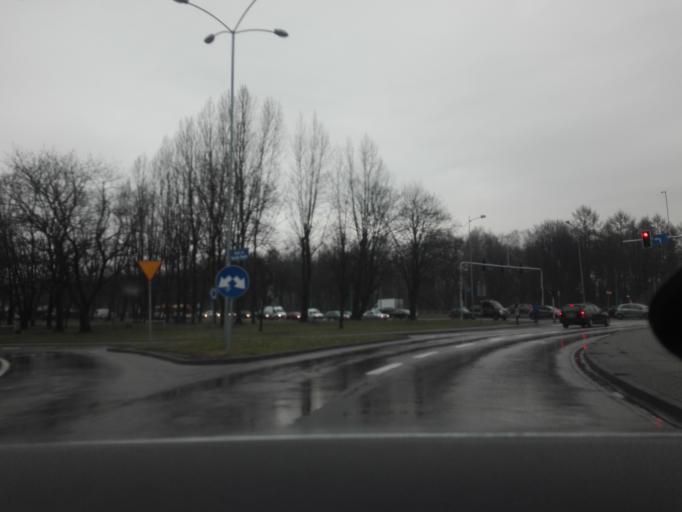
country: PL
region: Silesian Voivodeship
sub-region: Chorzow
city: Chorzow
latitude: 50.2761
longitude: 18.9842
